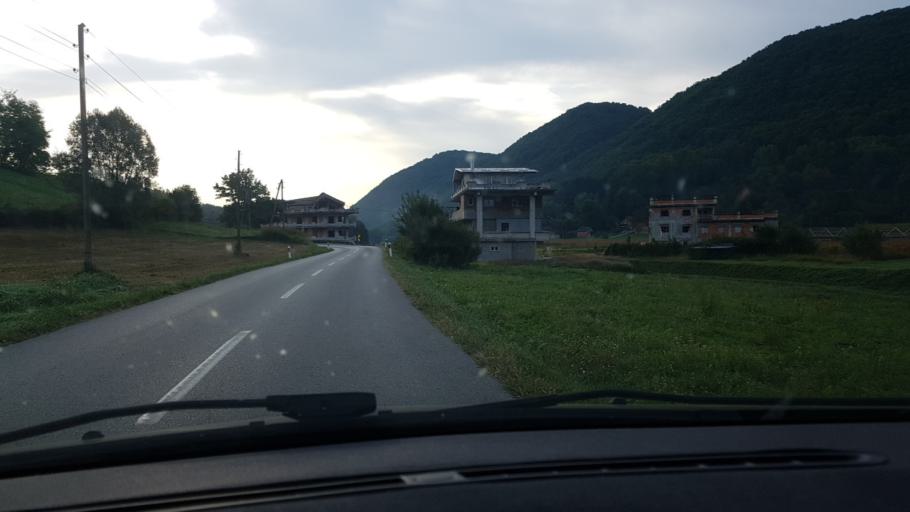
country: HR
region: Krapinsko-Zagorska
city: Mihovljan
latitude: 46.1244
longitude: 15.9842
